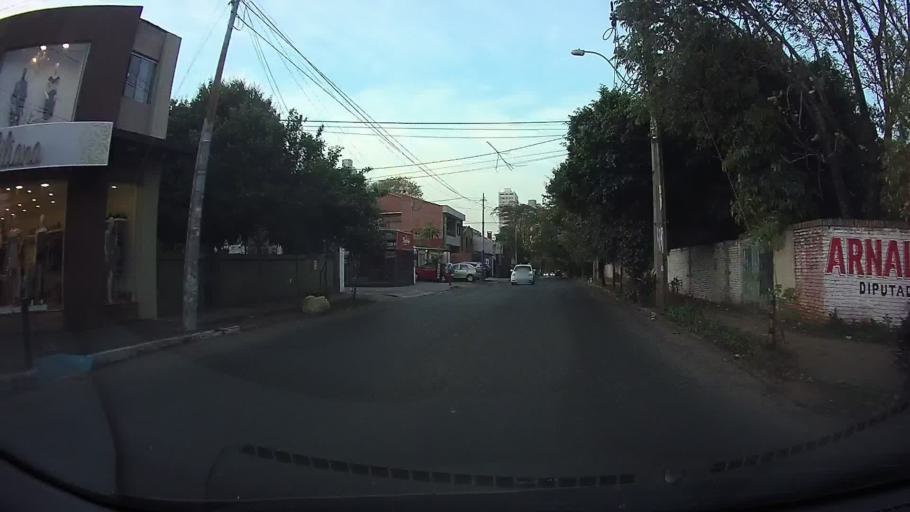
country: PY
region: Central
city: Fernando de la Mora
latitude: -25.2905
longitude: -57.5595
